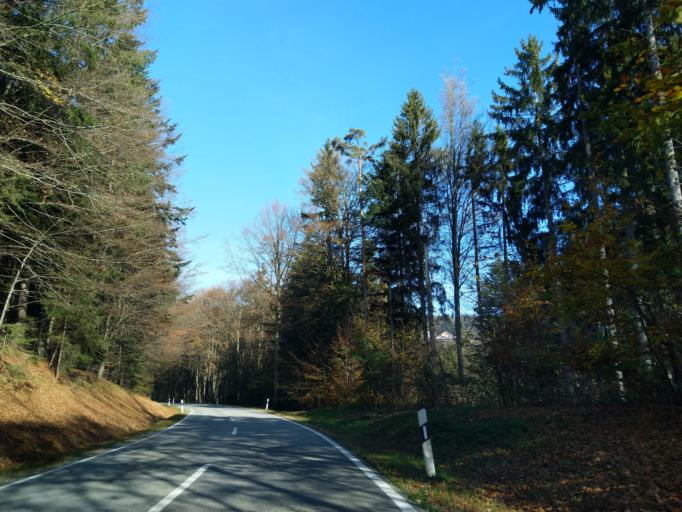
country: DE
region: Bavaria
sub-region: Lower Bavaria
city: Hunding
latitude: 48.8100
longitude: 13.1882
